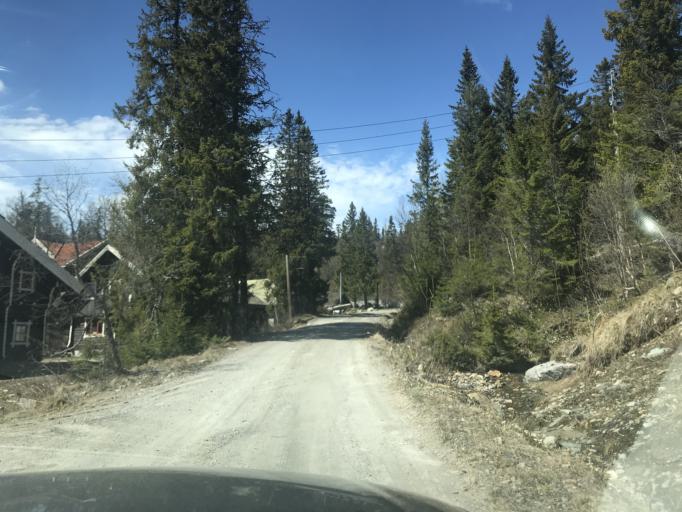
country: NO
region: Telemark
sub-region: Tinn
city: Rjukan
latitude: 59.7943
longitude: 8.7499
